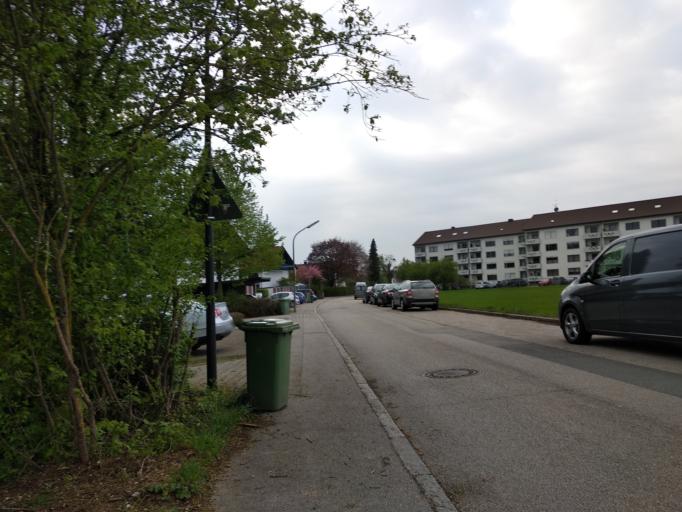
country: DE
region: Bavaria
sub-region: Upper Bavaria
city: Kirchseeon
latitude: 48.0785
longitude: 11.8641
